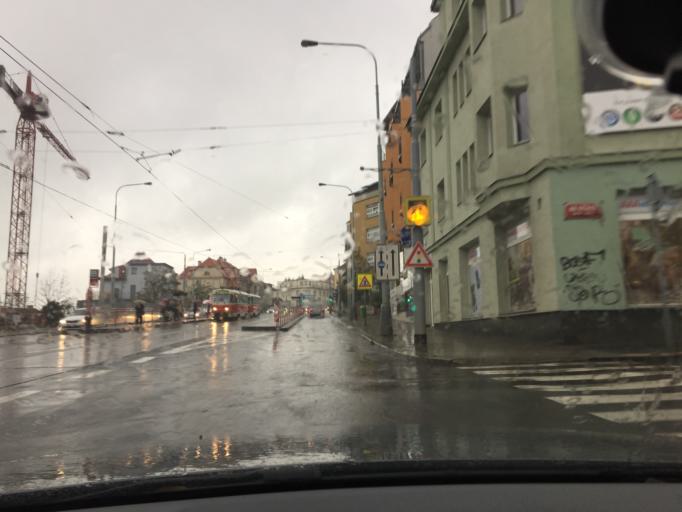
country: CZ
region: Praha
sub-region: Praha 8
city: Liben
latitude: 50.1196
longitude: 14.4614
